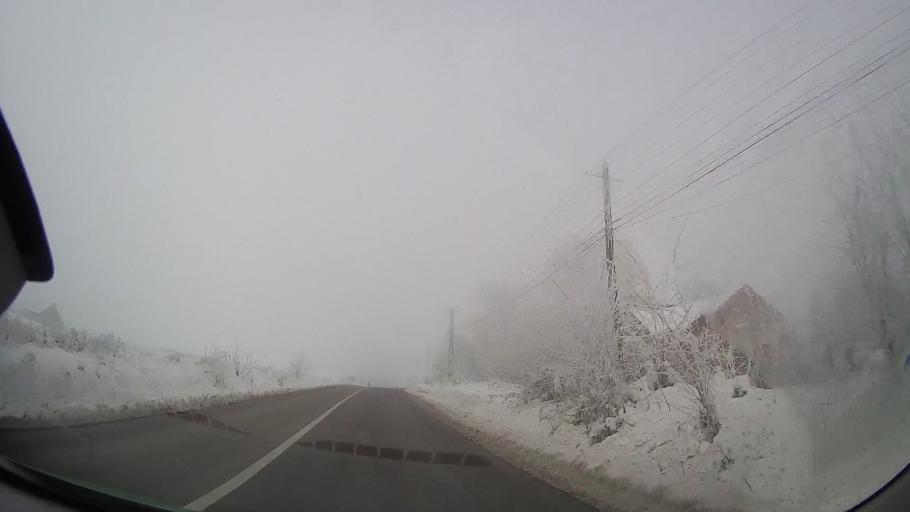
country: RO
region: Iasi
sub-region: Comuna Halaucesti
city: Halaucesti
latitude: 47.1027
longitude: 26.8146
